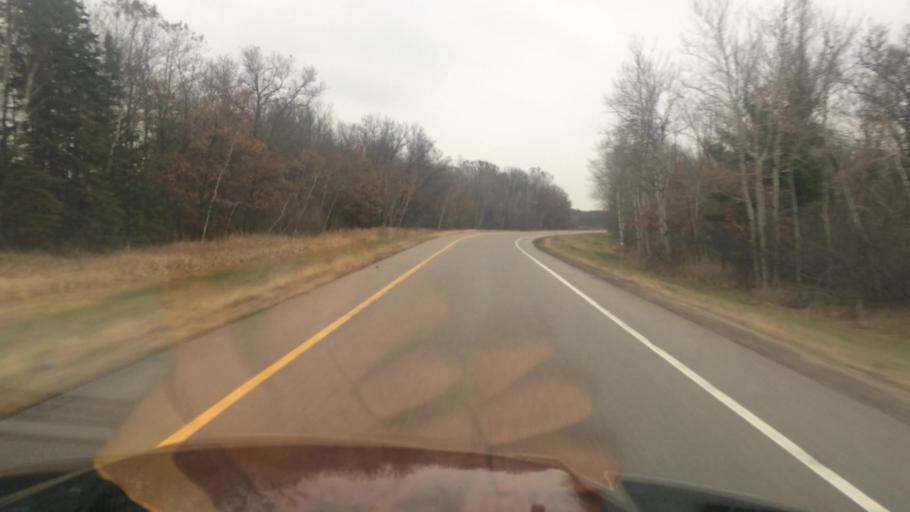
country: US
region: Wisconsin
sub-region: Portage County
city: Stevens Point
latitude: 44.5498
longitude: -89.5820
